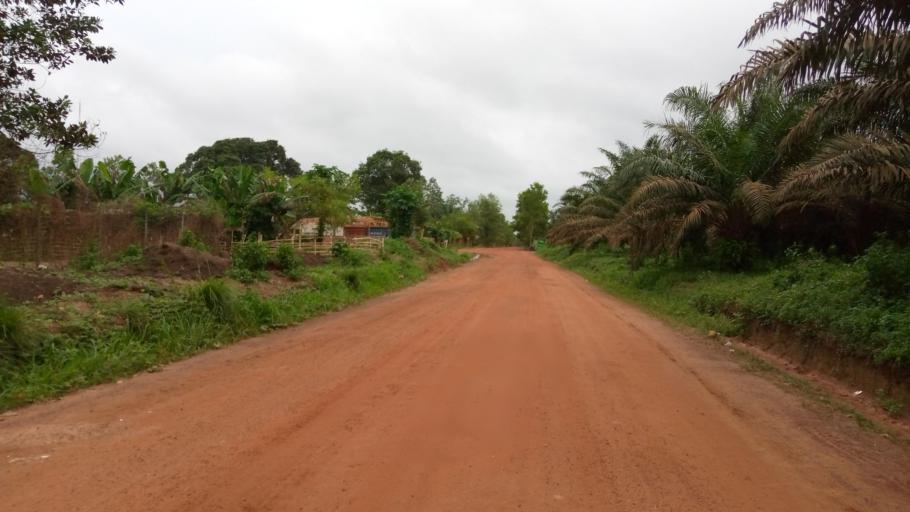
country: SL
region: Southern Province
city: Gandorhun
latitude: 7.4373
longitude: -11.8431
